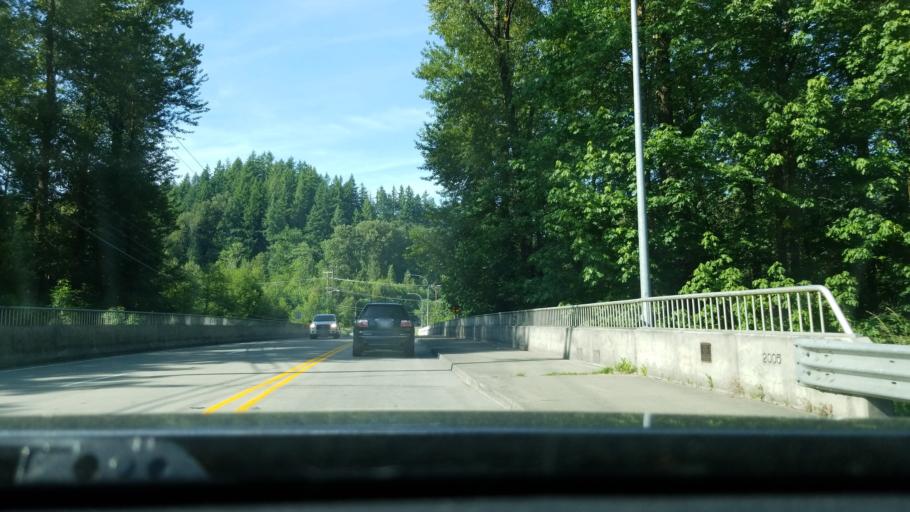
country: US
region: Washington
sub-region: King County
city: Fairwood
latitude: 47.4667
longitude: -122.1370
